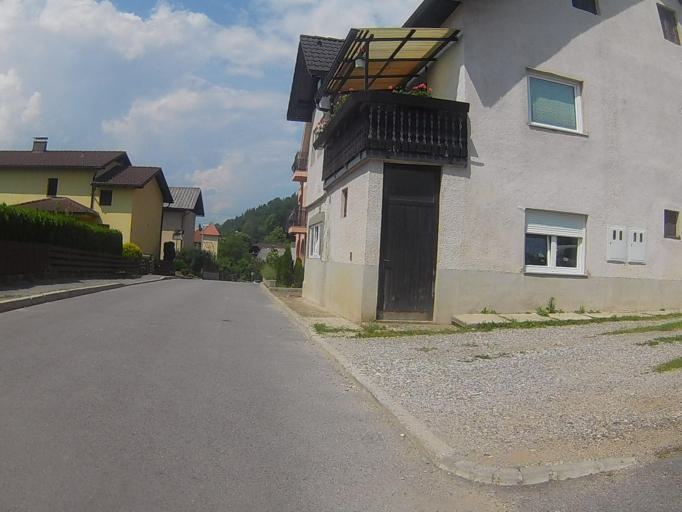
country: SI
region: Maribor
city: Bresternica
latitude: 46.5684
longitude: 15.5765
